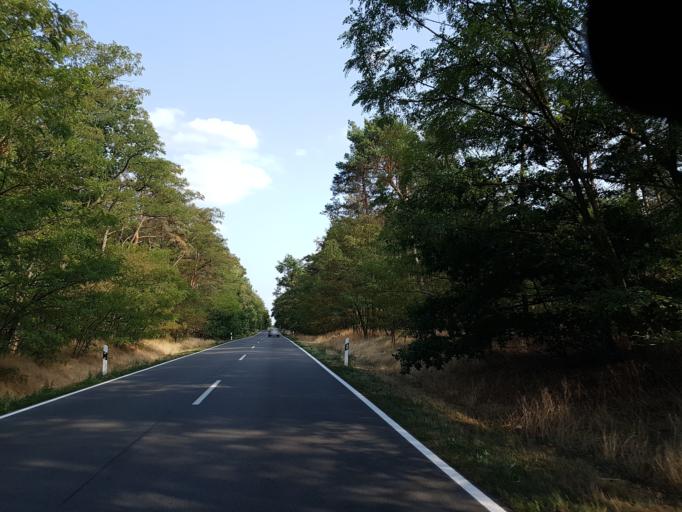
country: DE
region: Saxony-Anhalt
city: Pretzsch
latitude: 51.7343
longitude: 12.7671
